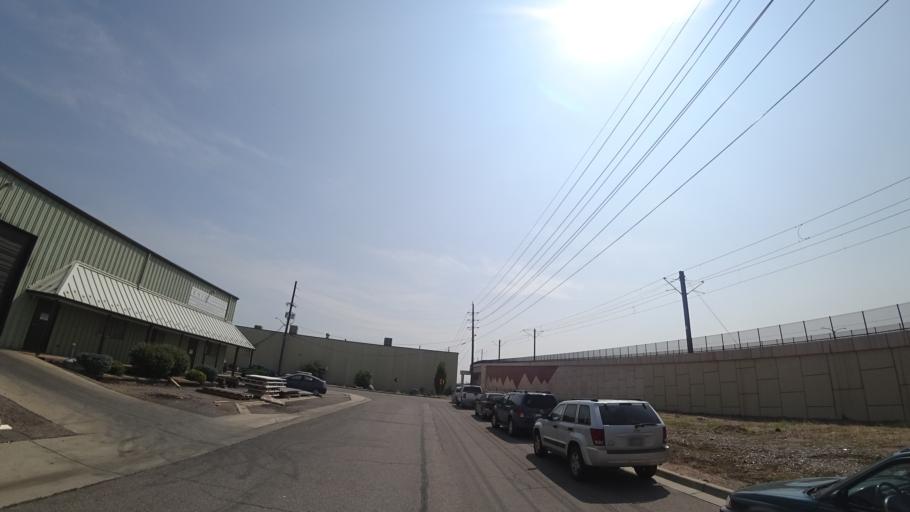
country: US
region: Colorado
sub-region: Arapahoe County
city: Littleton
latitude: 39.6336
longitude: -105.0073
